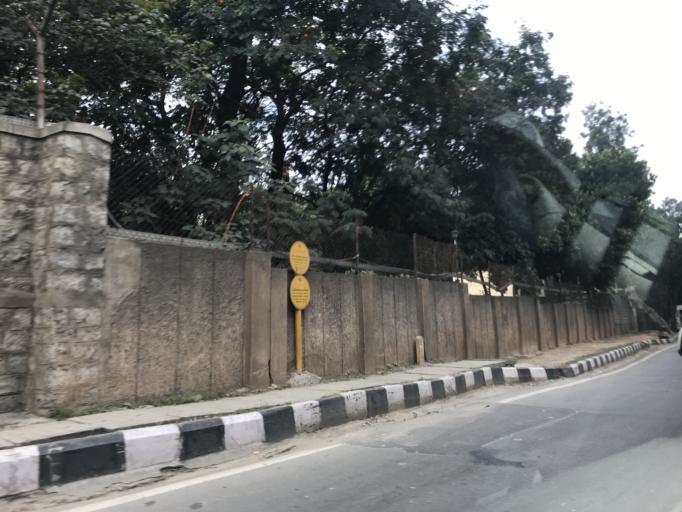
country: IN
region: Karnataka
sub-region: Bangalore Urban
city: Bangalore
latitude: 13.0149
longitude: 77.5642
